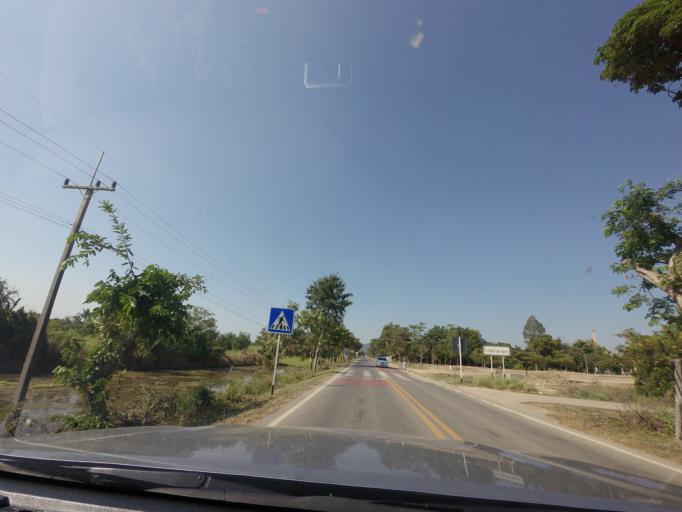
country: TH
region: Sukhothai
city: Sawankhalok
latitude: 17.3724
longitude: 99.8006
